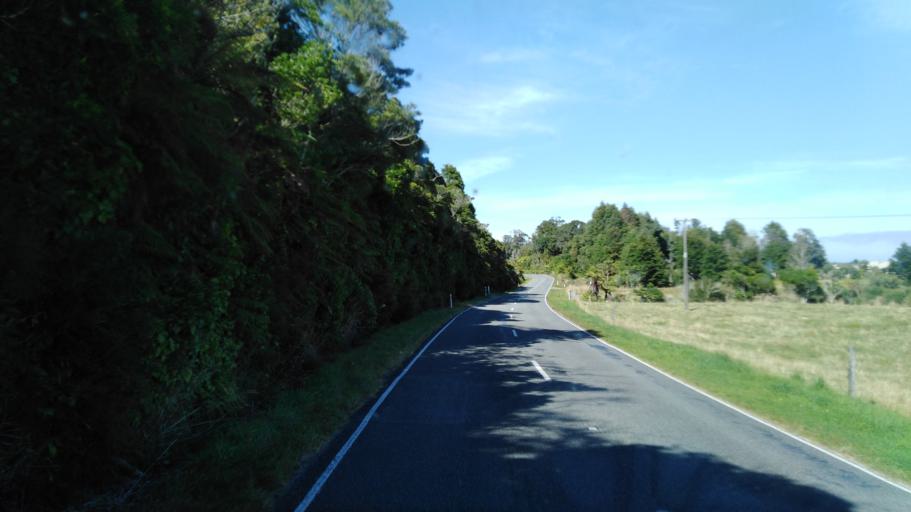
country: NZ
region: West Coast
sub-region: Buller District
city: Westport
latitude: -41.2682
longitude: 172.1111
